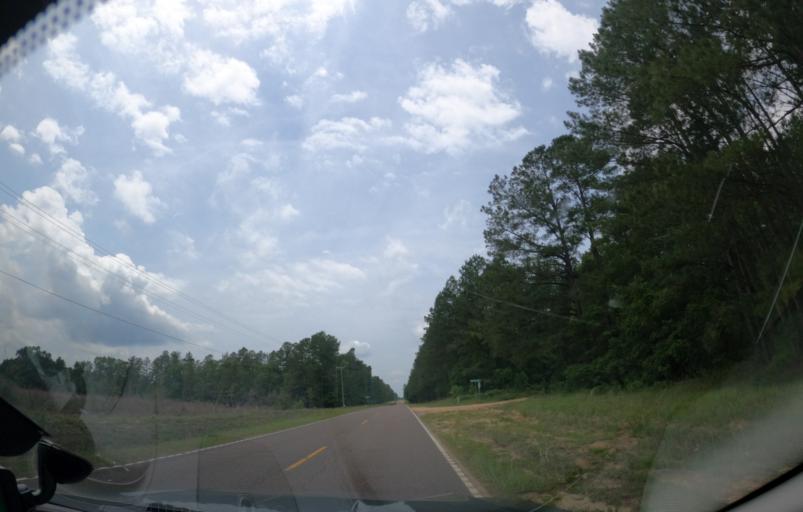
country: US
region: South Carolina
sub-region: Barnwell County
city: Williston
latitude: 33.5754
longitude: -81.4454
